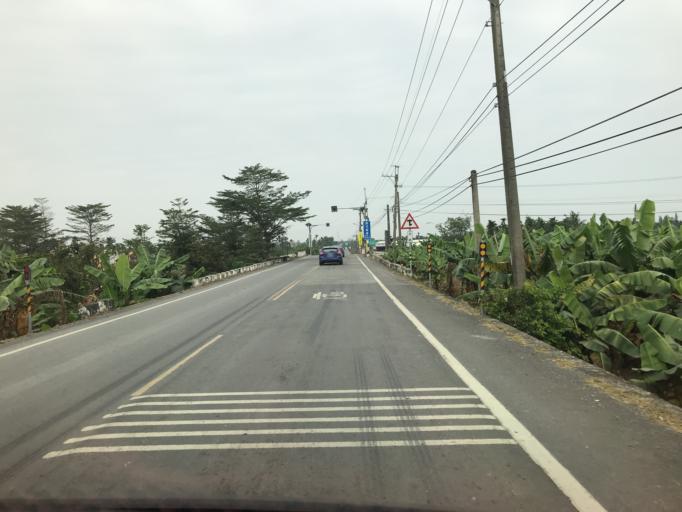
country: TW
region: Taiwan
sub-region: Pingtung
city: Pingtung
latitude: 22.4675
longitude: 120.6096
